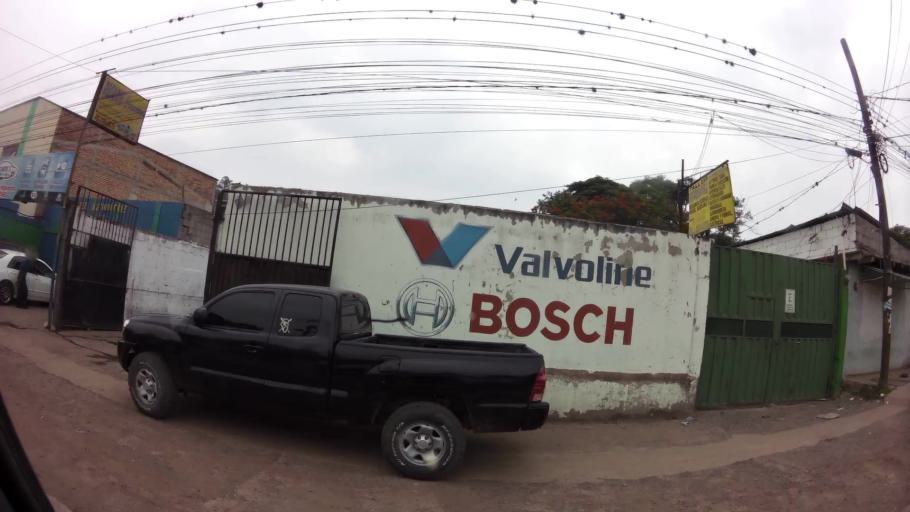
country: HN
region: Francisco Morazan
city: Tegucigalpa
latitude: 14.0668
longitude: -87.2116
